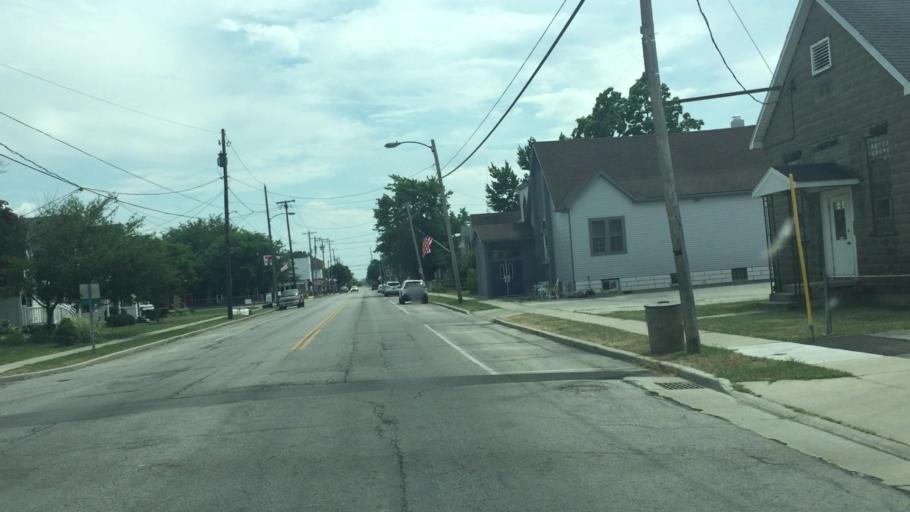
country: US
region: Ohio
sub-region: Wood County
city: Walbridge
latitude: 41.5900
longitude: -83.4934
